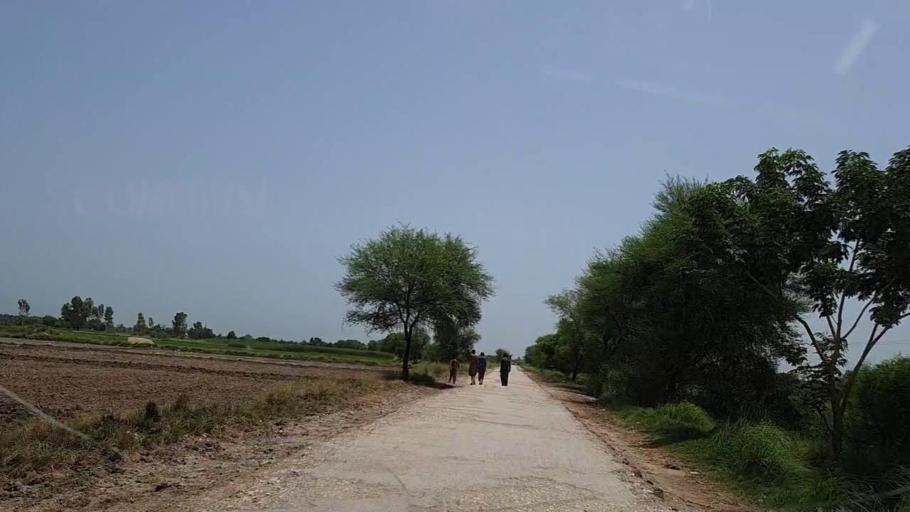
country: PK
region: Sindh
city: Tharu Shah
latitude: 26.9535
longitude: 68.0849
